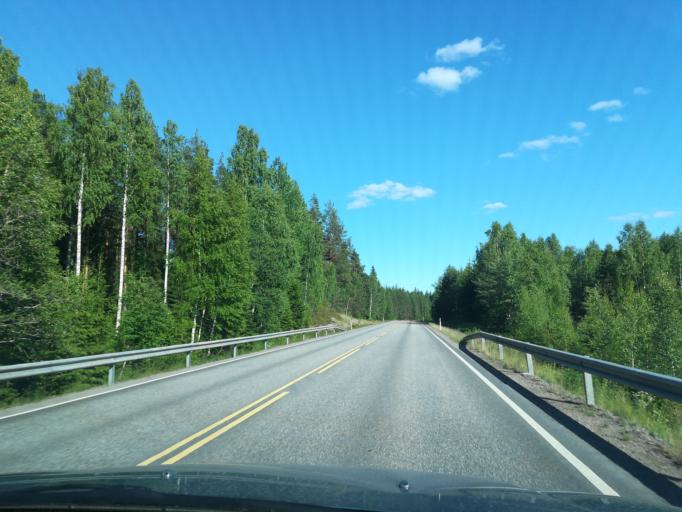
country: FI
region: South Karelia
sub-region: Imatra
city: Ruokolahti
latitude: 61.3906
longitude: 28.6431
